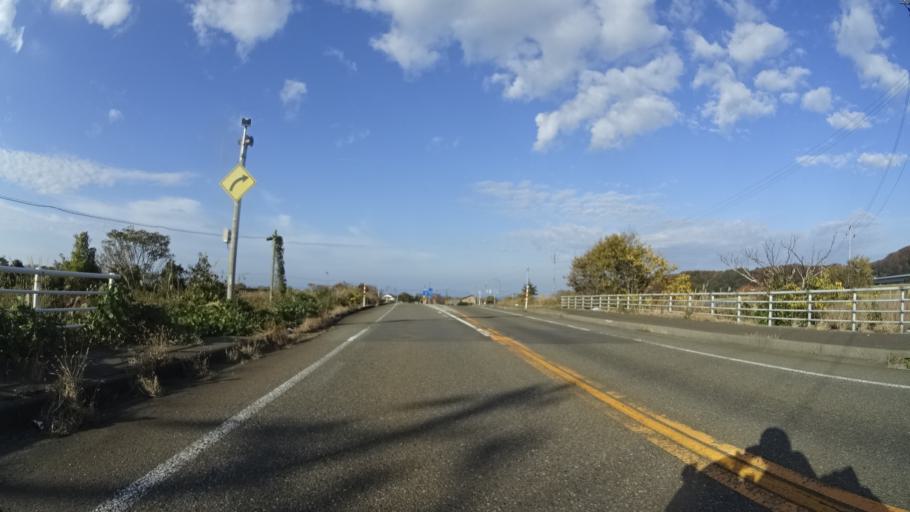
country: JP
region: Niigata
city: Kashiwazaki
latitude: 37.3274
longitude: 138.4558
